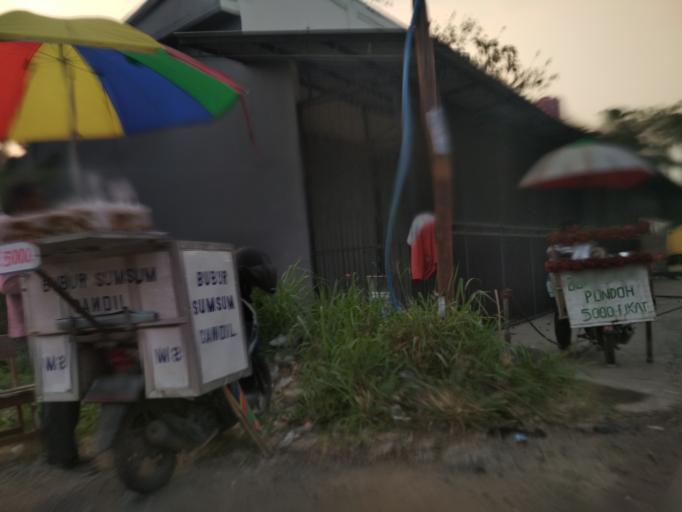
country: ID
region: West Java
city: Caringin
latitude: -6.6635
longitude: 106.8452
